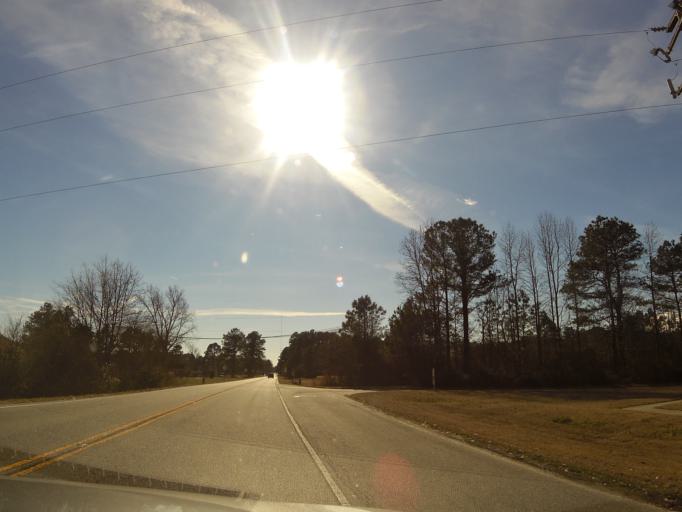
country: US
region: Virginia
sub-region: Isle of Wight County
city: Windsor
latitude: 36.8238
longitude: -76.7455
